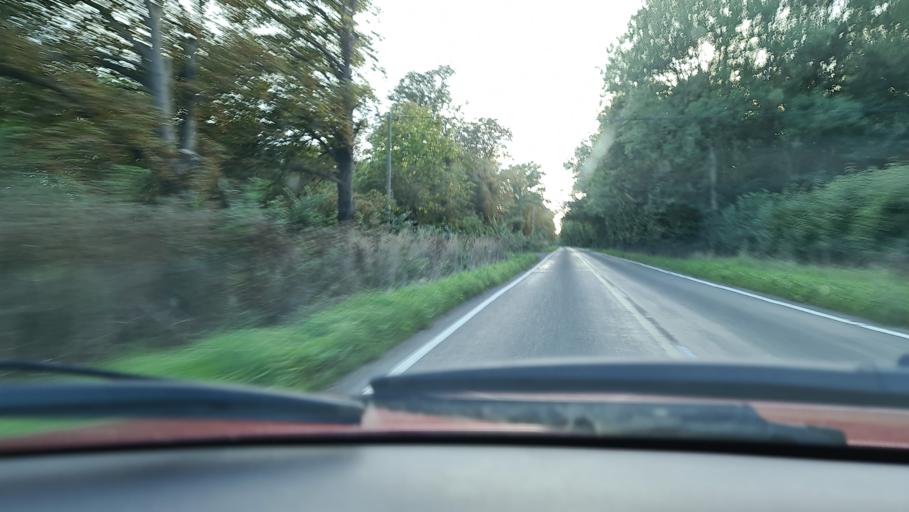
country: GB
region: England
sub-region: Oxfordshire
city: Somerton
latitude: 51.8939
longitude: -1.2304
